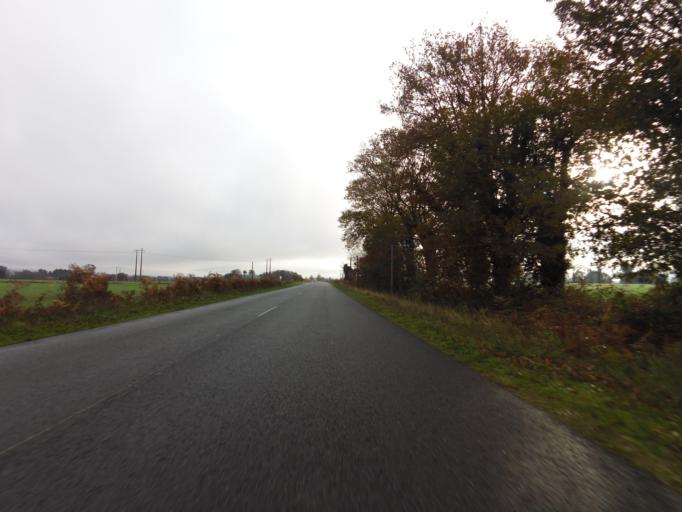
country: FR
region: Brittany
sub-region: Departement du Morbihan
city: Saint-Martin-sur-Oust
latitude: 47.7202
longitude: -2.2500
